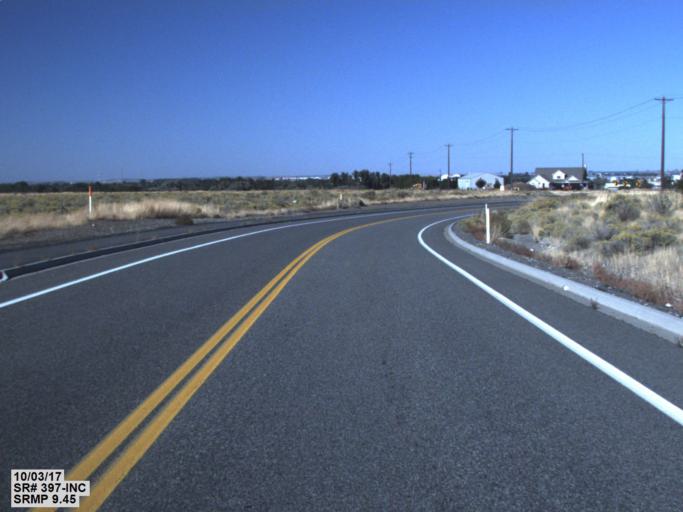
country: US
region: Washington
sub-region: Benton County
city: Finley
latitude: 46.1362
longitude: -119.0346
